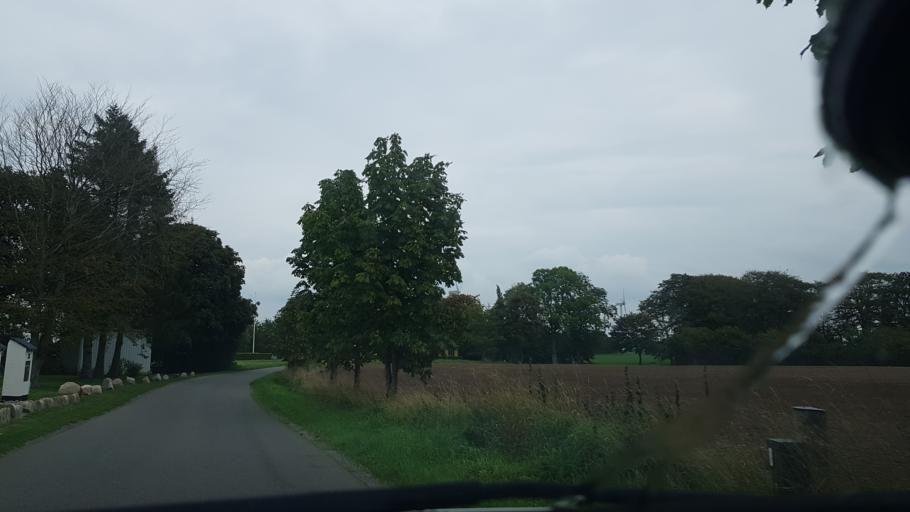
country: DK
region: South Denmark
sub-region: Vejle Kommune
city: Egtved
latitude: 55.5722
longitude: 9.2960
